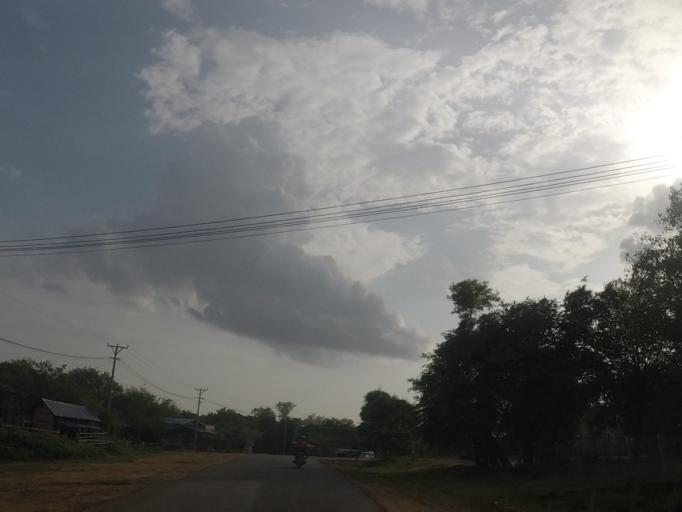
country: MM
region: Mandalay
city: Meiktila
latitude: 20.5096
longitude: 95.7390
